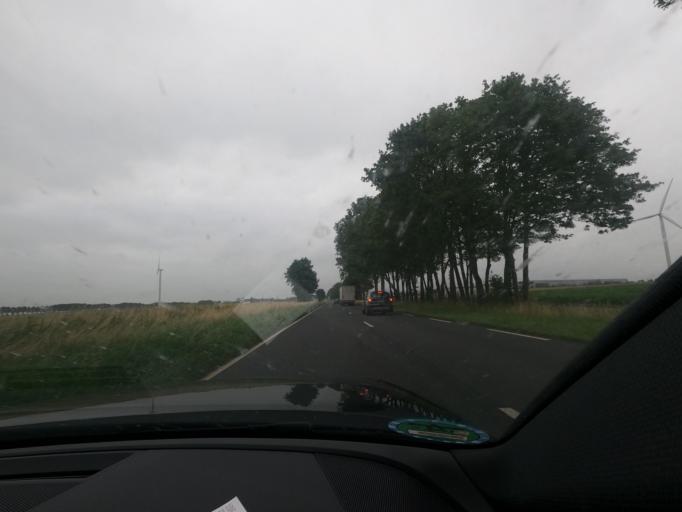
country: FR
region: Picardie
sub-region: Departement de la Somme
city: Roye
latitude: 49.7137
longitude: 2.7528
